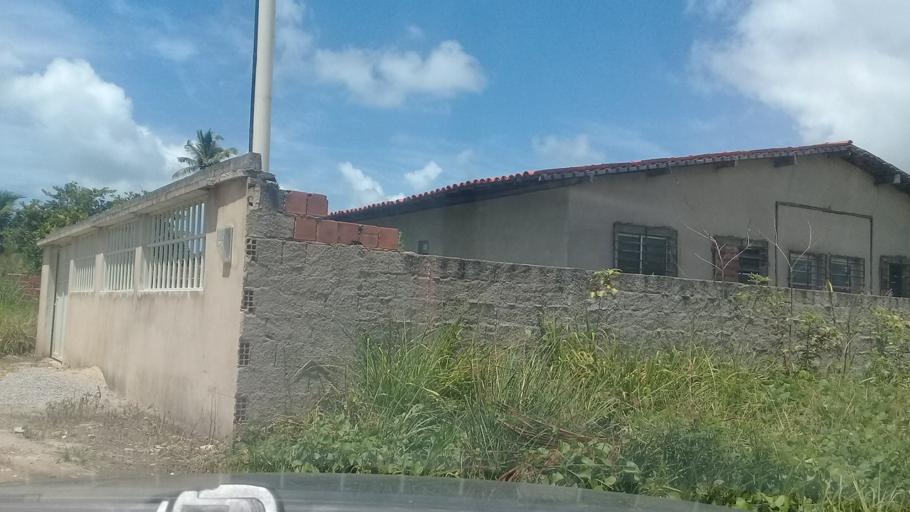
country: BR
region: Pernambuco
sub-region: Sirinhaem
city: Sirinhaem
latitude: -8.6212
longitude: -35.0652
